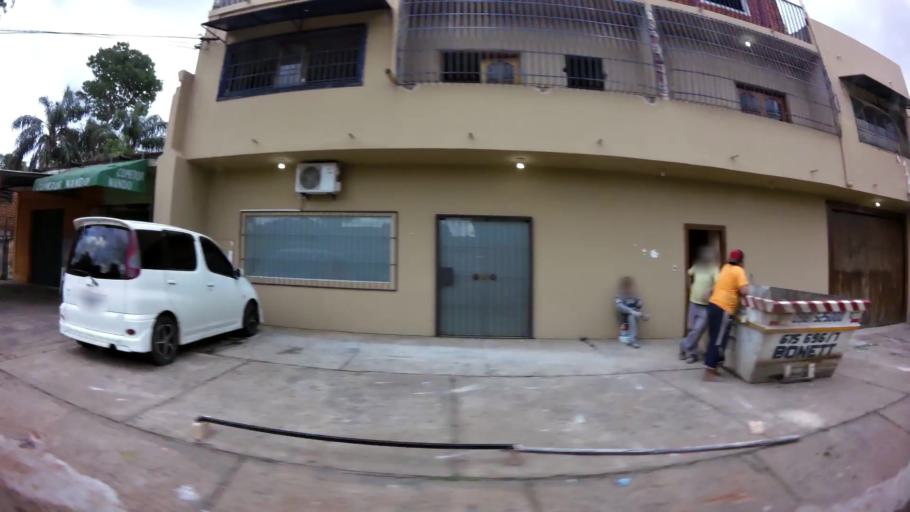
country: PY
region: Central
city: Fernando de la Mora
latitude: -25.3330
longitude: -57.5535
